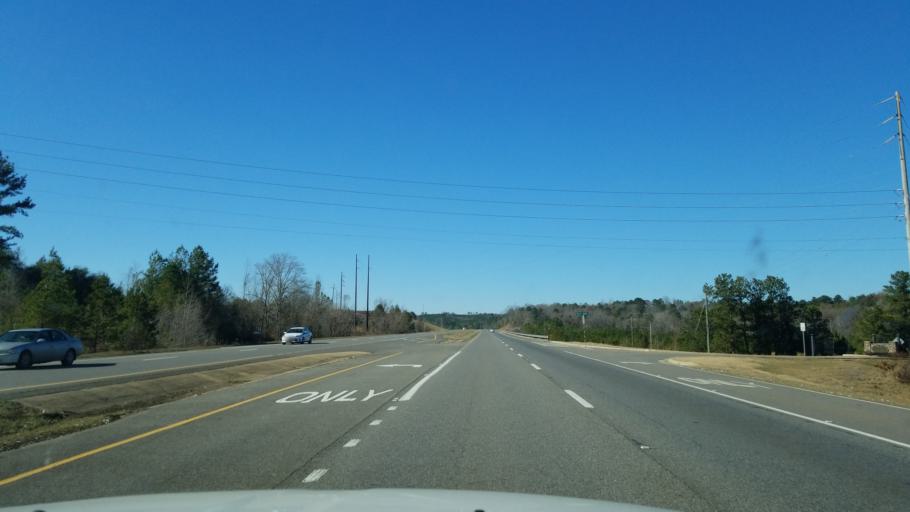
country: US
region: Alabama
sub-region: Tuscaloosa County
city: Northport
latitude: 33.2603
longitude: -87.7025
